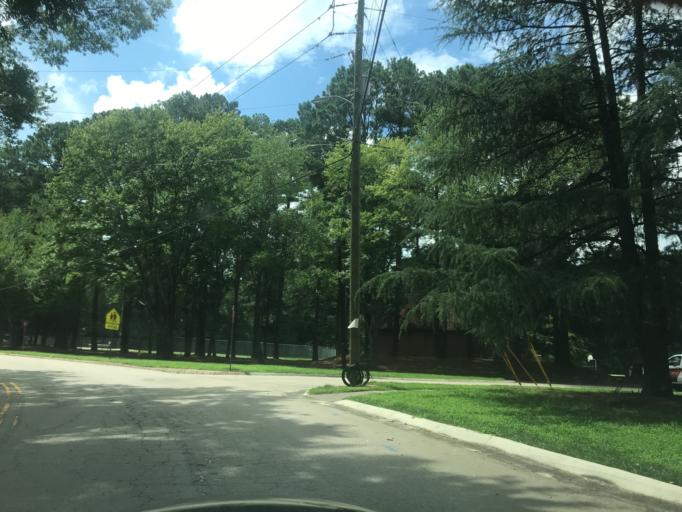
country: US
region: North Carolina
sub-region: Wake County
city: Raleigh
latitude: 35.8149
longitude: -78.6306
